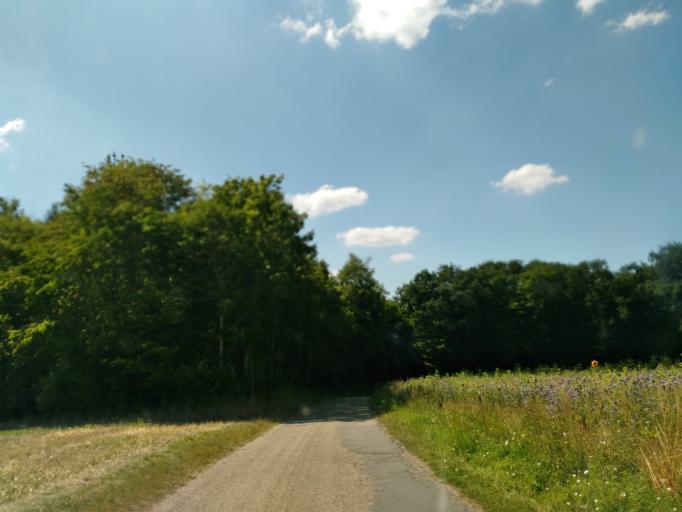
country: DE
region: Baden-Wuerttemberg
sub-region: Karlsruhe Region
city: Limbach
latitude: 49.4556
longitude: 9.2309
